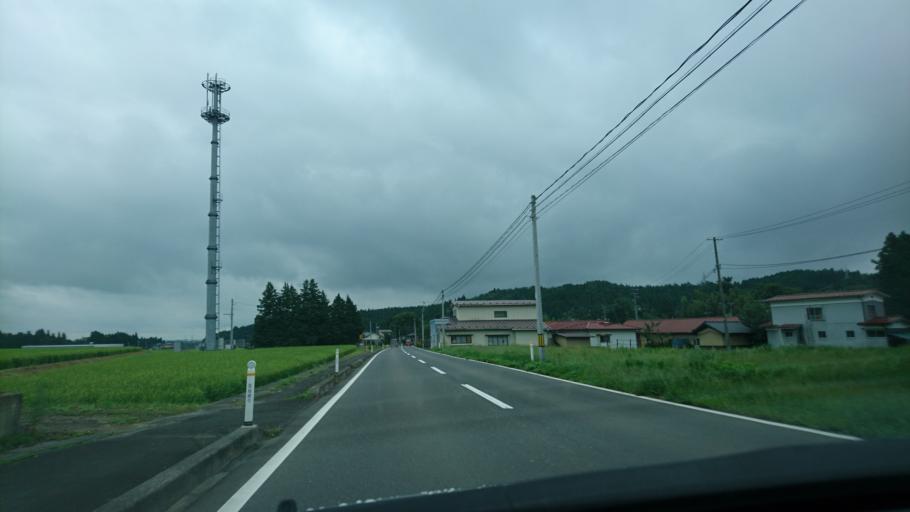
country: JP
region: Iwate
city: Ichinoseki
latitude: 38.8047
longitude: 140.9357
